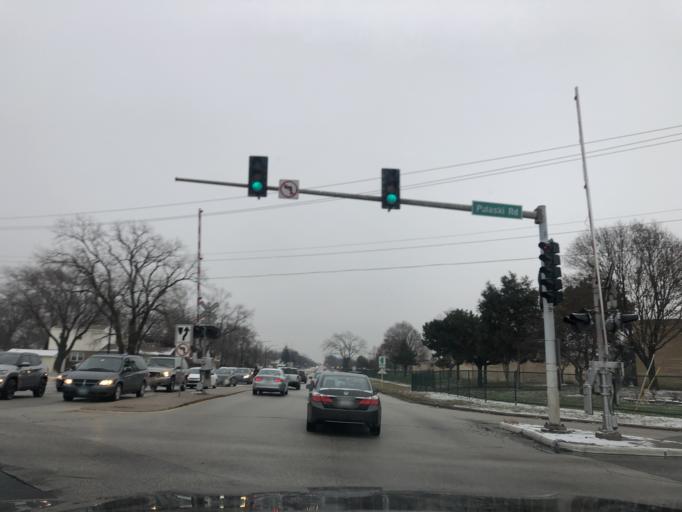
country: US
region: Illinois
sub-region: Cook County
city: Hometown
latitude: 41.7348
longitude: -87.7216
